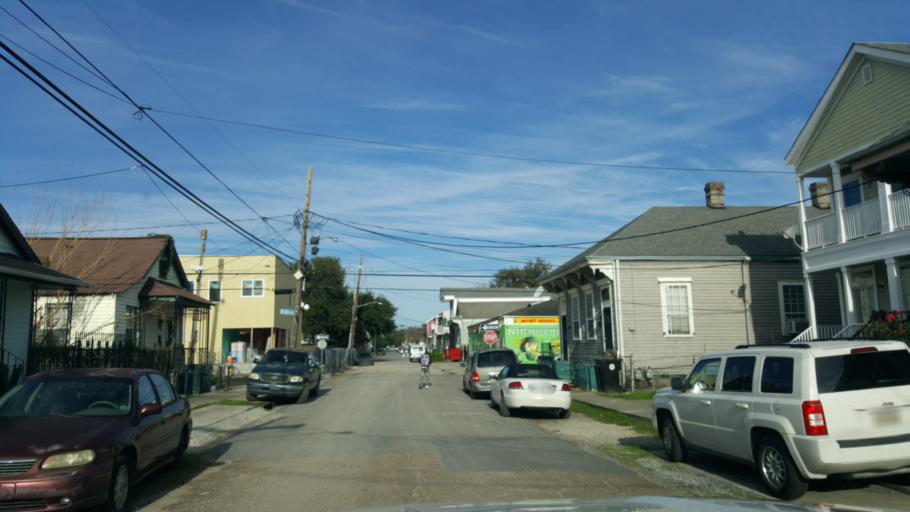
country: US
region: Louisiana
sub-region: Orleans Parish
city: New Orleans
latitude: 29.9701
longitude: -90.0731
